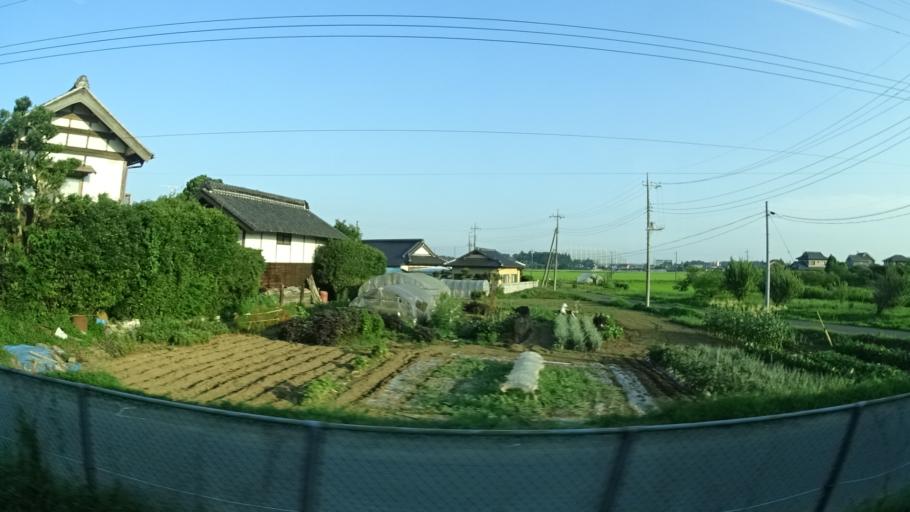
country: JP
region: Ibaraki
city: Tomobe
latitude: 36.3596
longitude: 140.3287
